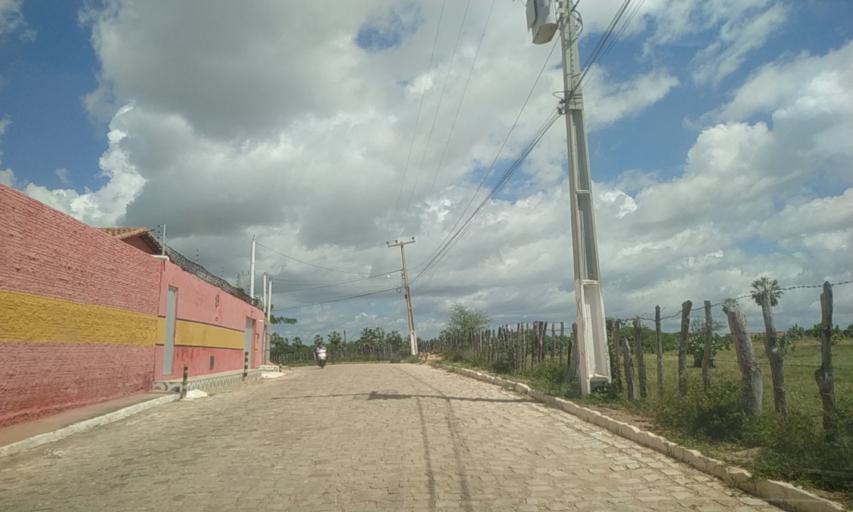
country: BR
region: Rio Grande do Norte
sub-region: Areia Branca
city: Areia Branca
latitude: -4.9305
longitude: -37.1101
